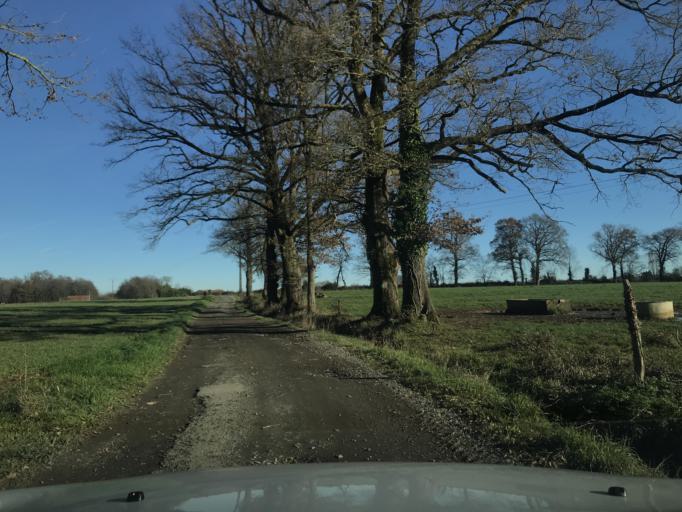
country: FR
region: Poitou-Charentes
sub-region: Departement de la Charente
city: Saint-Claud
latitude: 45.8545
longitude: 0.5029
